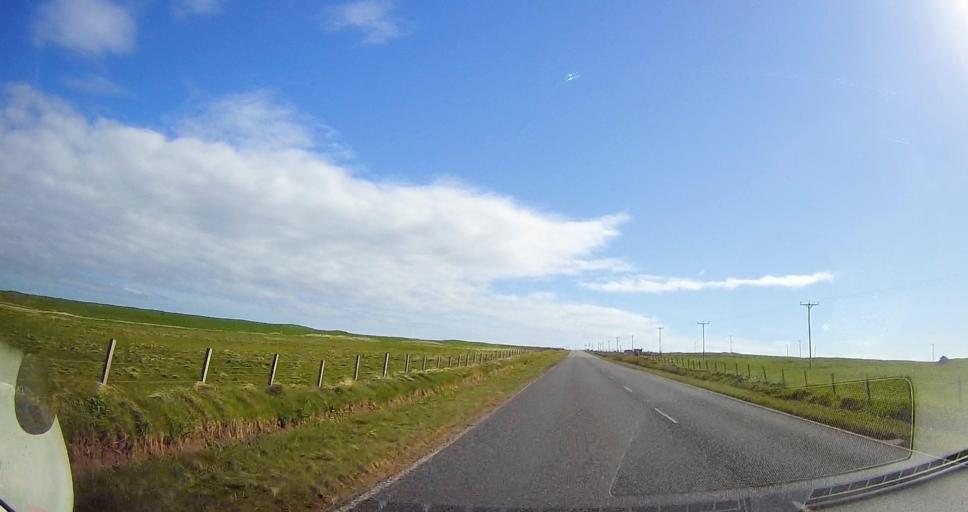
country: GB
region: Scotland
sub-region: Shetland Islands
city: Sandwick
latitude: 59.9035
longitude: -1.3028
